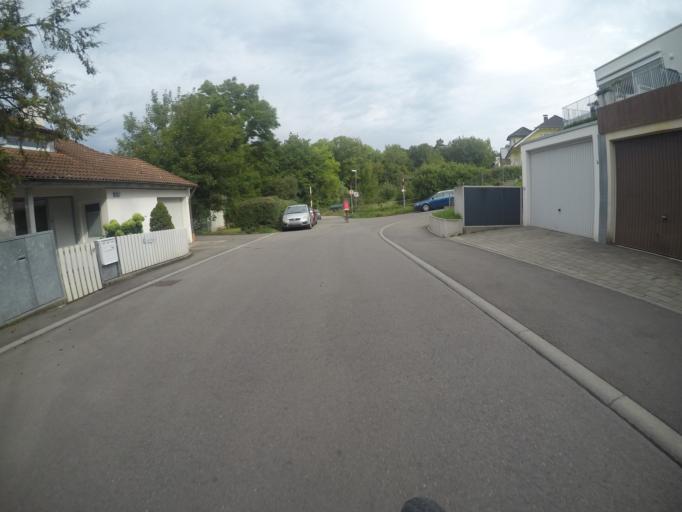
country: DE
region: Baden-Wuerttemberg
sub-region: Regierungsbezirk Stuttgart
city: Stuttgart
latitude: 48.7449
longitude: 9.1459
